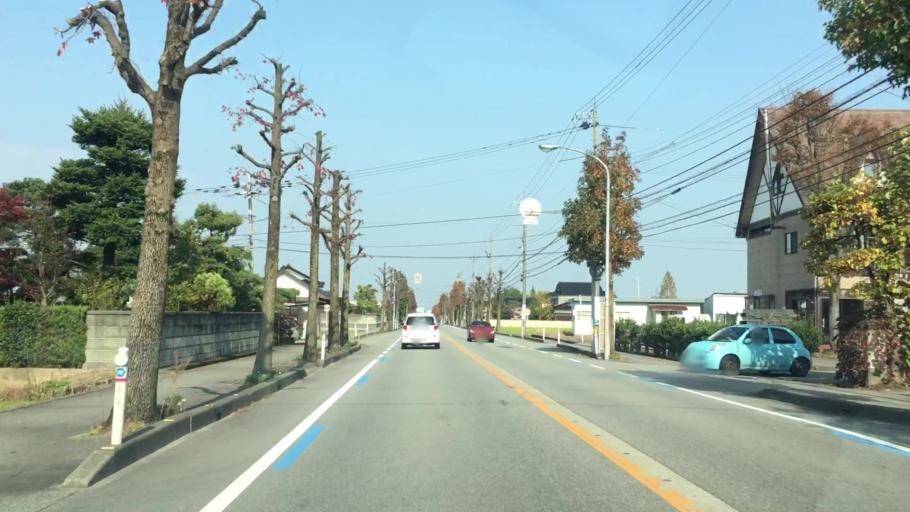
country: JP
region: Toyama
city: Toyama-shi
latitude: 36.6369
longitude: 137.1938
